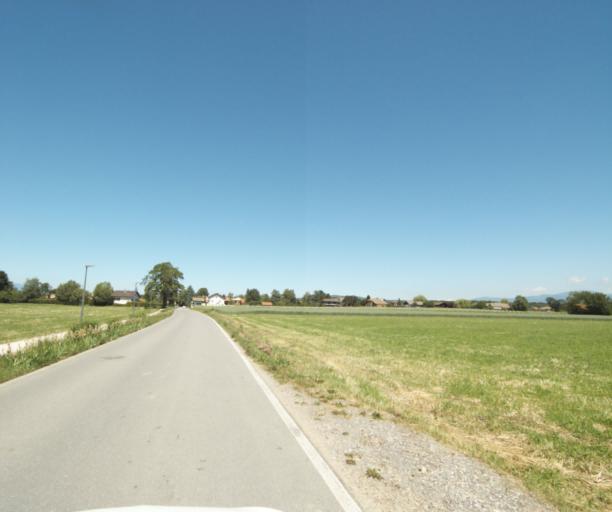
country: FR
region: Rhone-Alpes
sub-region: Departement de la Haute-Savoie
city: Veigy-Foncenex
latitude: 46.2553
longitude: 6.2620
